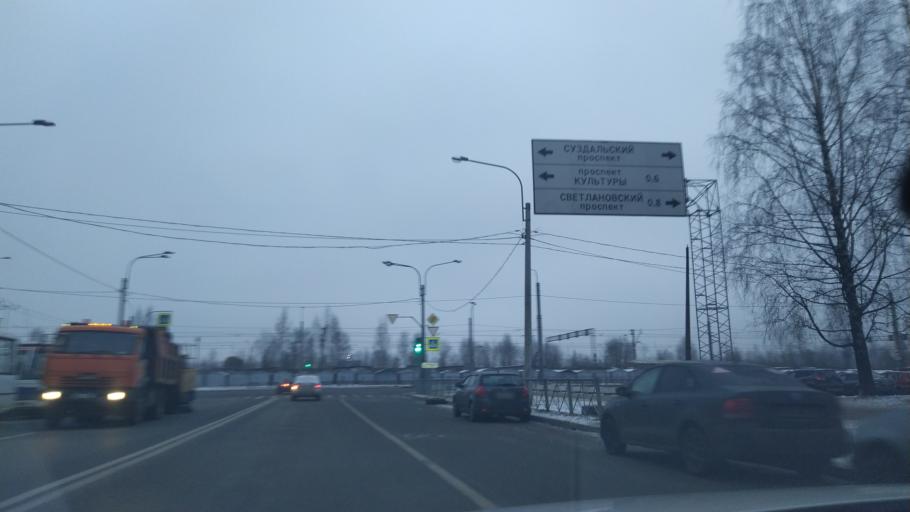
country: RU
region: St.-Petersburg
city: Grazhdanka
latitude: 60.0496
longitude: 30.3924
